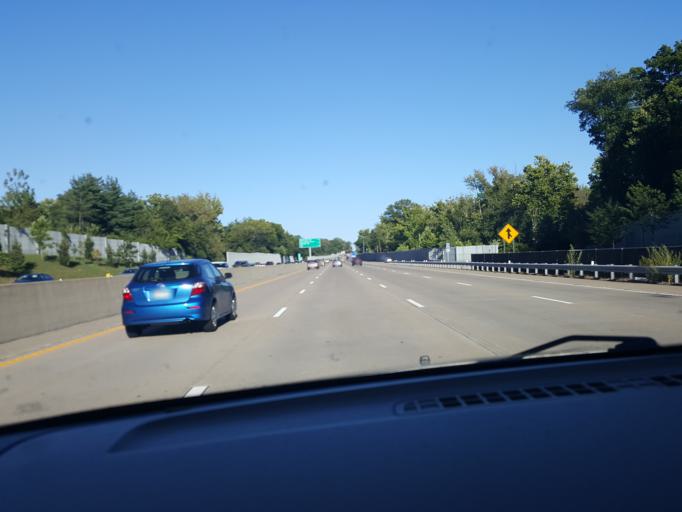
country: US
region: Missouri
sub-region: Saint Louis County
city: Ladue
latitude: 38.6315
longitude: -90.3804
